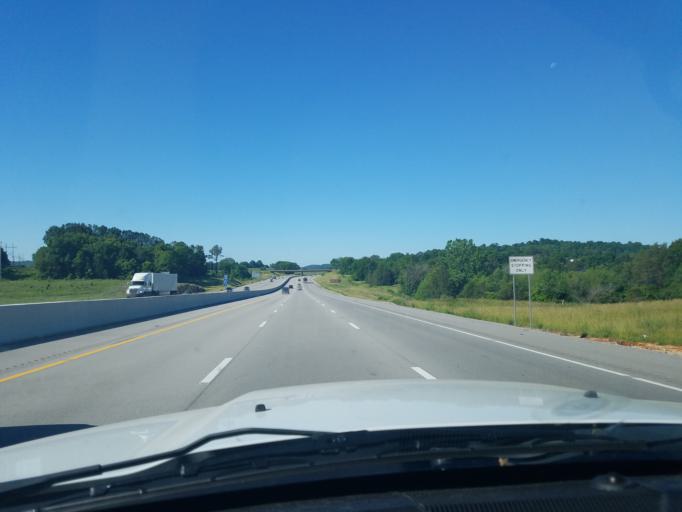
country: US
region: Kentucky
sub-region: Hart County
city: Munfordville
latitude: 37.2806
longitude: -85.9099
